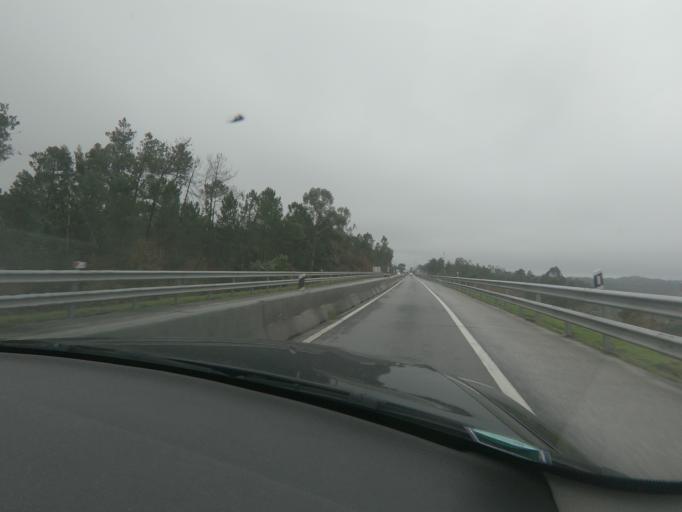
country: PT
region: Viseu
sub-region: Concelho de Tondela
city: Tondela
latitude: 40.5900
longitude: -8.0135
